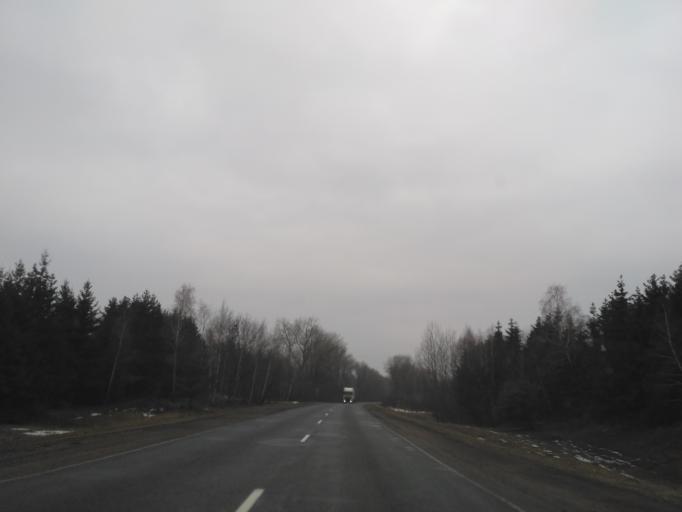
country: BY
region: Minsk
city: Snow
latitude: 53.2667
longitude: 26.3302
